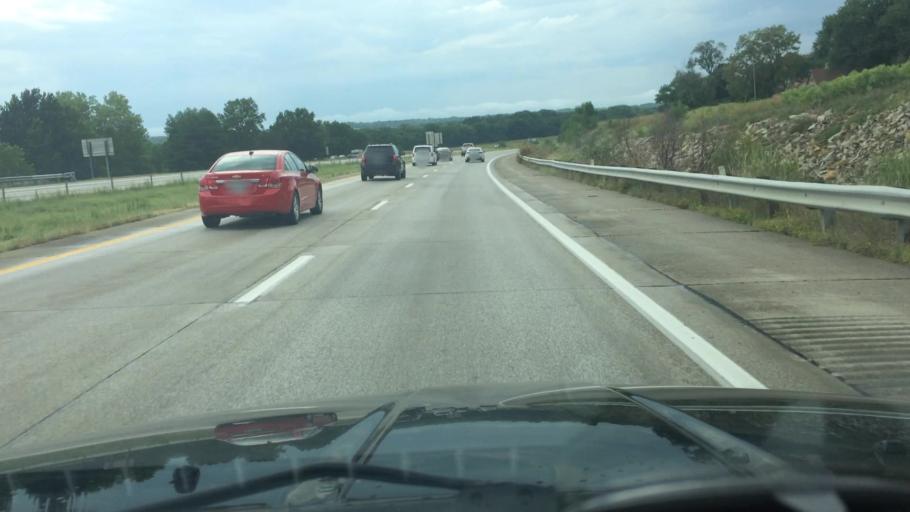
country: US
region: Missouri
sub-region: Cass County
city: Harrisonville
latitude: 38.6633
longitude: -94.3861
